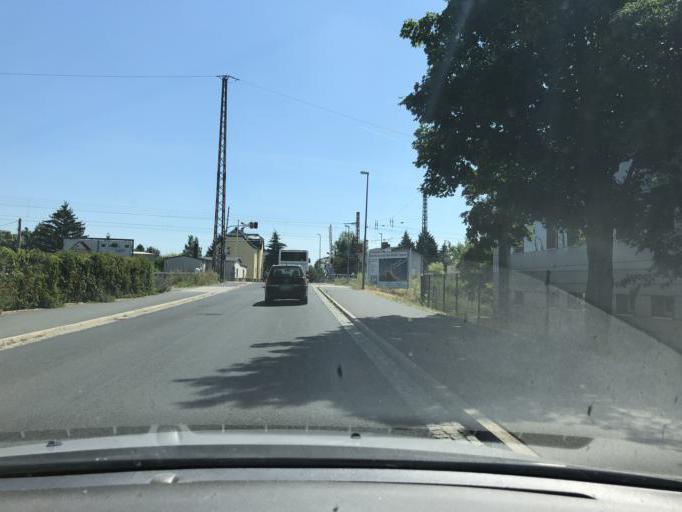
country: DE
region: Saxony
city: Coswig
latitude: 51.1109
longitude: 13.5979
